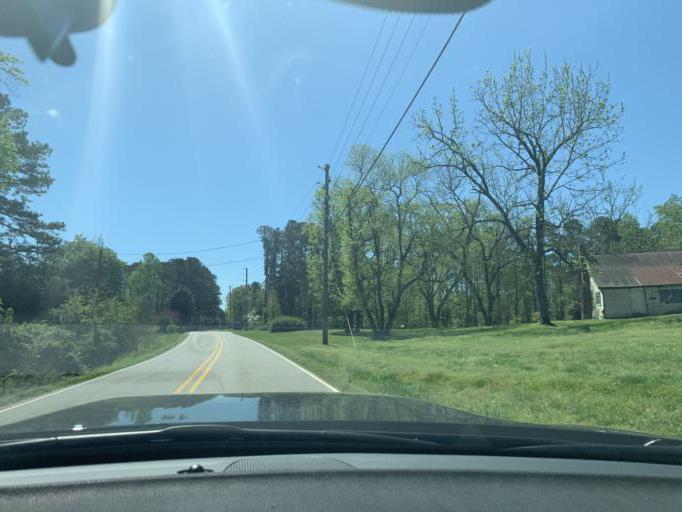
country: US
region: Georgia
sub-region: Forsyth County
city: Cumming
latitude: 34.1847
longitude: -84.1718
